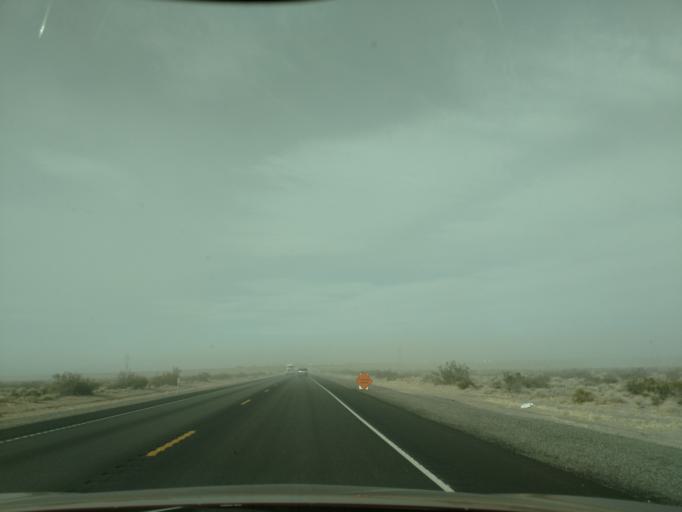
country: US
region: Nevada
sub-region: Nye County
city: Beatty
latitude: 36.6365
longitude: -116.3705
